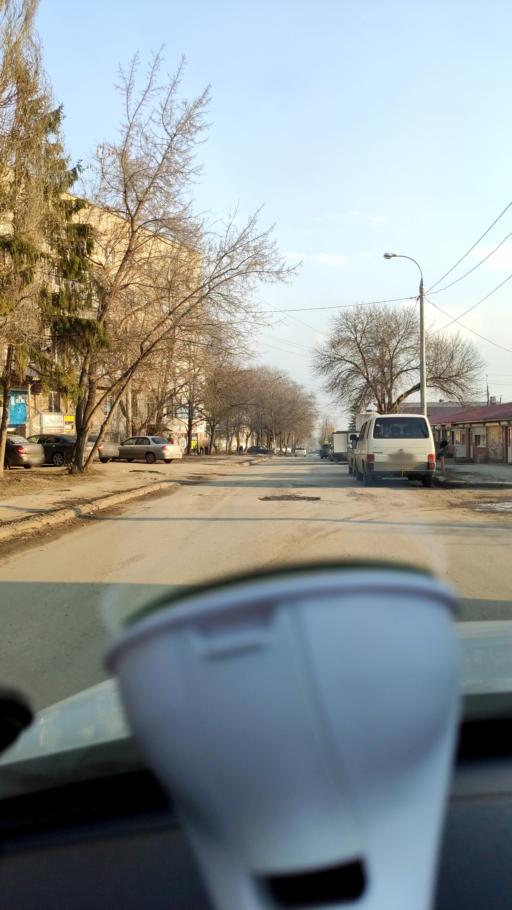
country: RU
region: Samara
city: Petra-Dubrava
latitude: 53.2994
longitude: 50.2772
